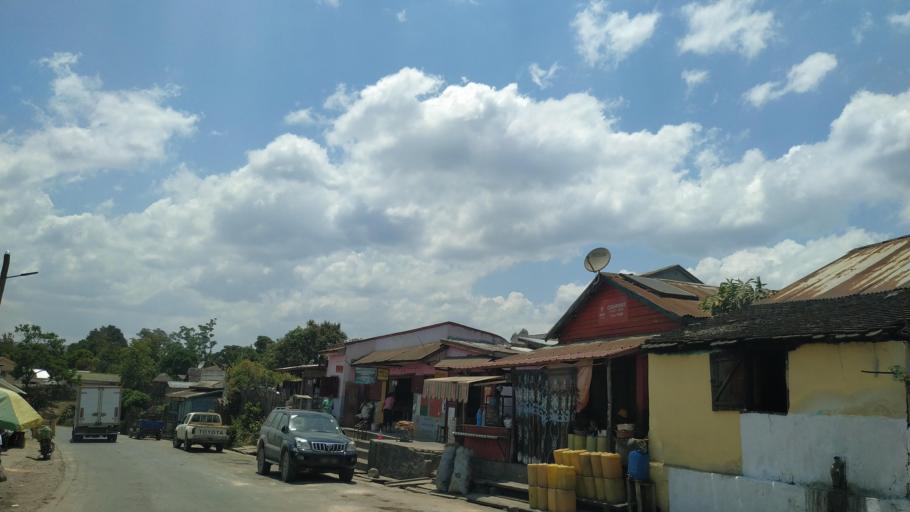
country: MG
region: Analamanga
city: Anjozorobe
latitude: -18.4428
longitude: 48.2638
